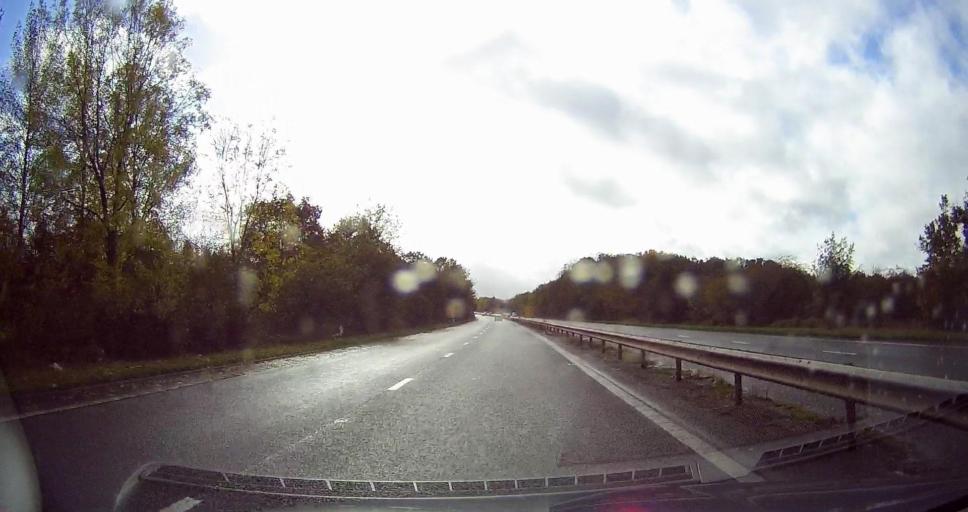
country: GB
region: England
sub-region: Warwickshire
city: Curdworth
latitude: 52.5452
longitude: -1.7775
